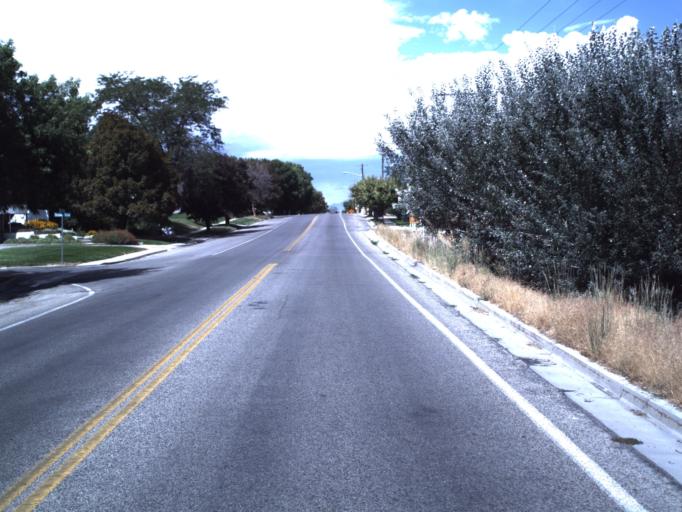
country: US
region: Utah
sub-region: Box Elder County
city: Tremonton
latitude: 41.7160
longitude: -112.1618
